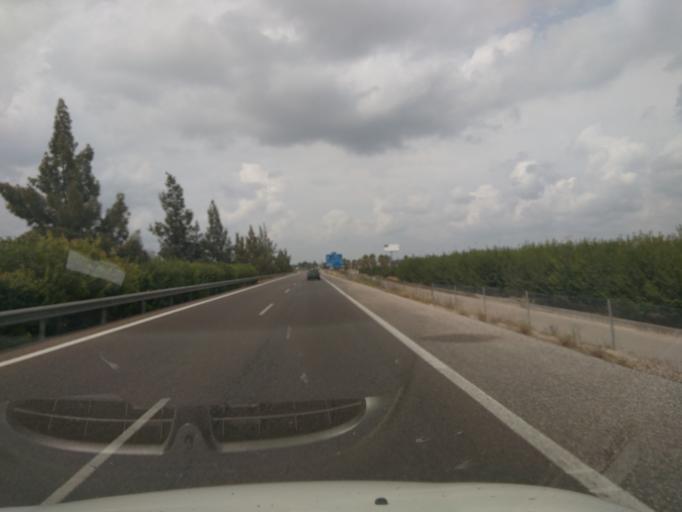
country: ES
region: Valencia
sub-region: Provincia de Valencia
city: Guadassuar
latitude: 39.1716
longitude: -0.4650
